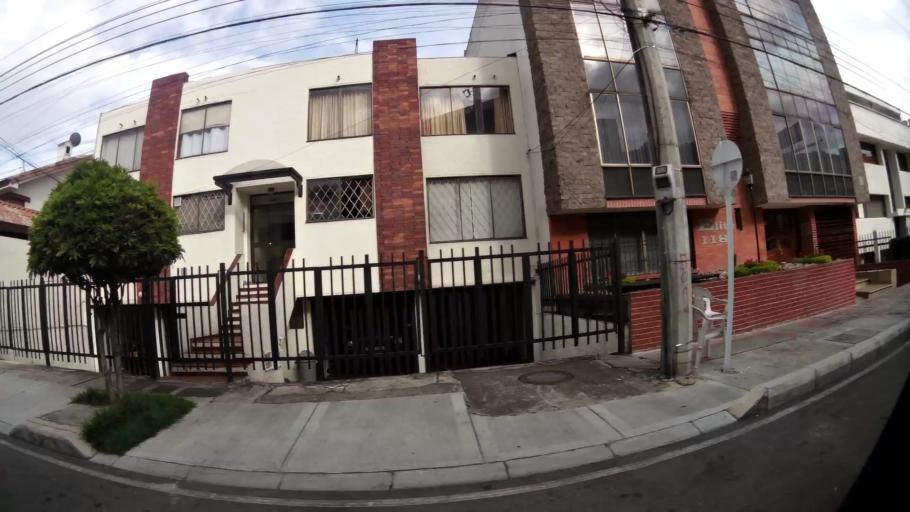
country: CO
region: Bogota D.C.
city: Barrio San Luis
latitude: 4.6962
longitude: -74.0344
